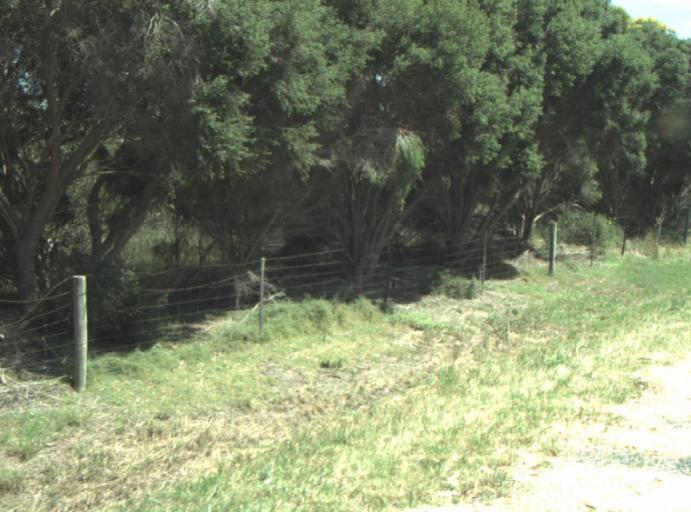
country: AU
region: Victoria
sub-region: Greater Geelong
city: Leopold
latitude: -38.1620
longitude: 144.4558
